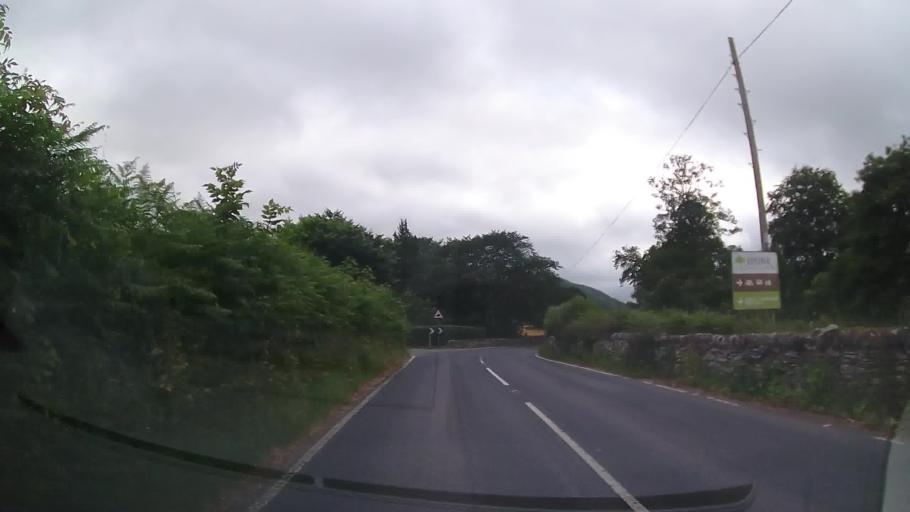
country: GB
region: Wales
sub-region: Denbighshire
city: Llandrillo
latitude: 52.9362
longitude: -3.4260
